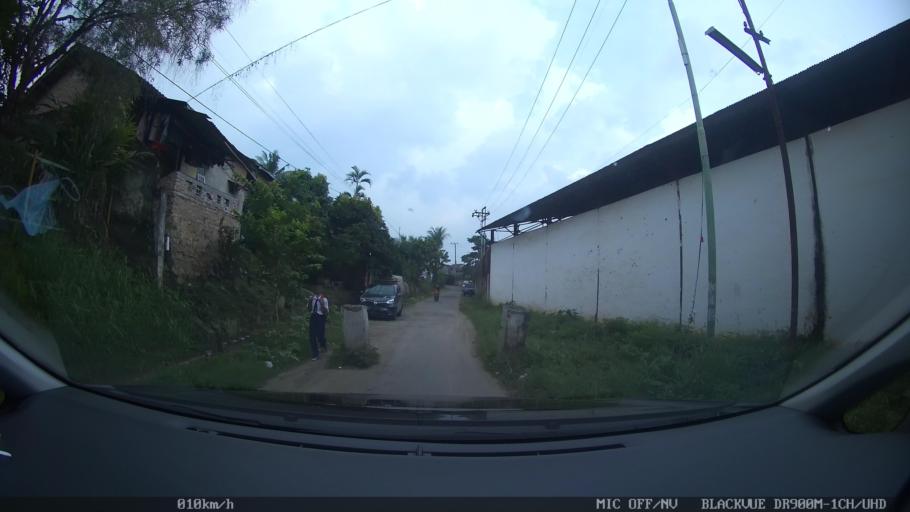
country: ID
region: Lampung
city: Bandarlampung
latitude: -5.4369
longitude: 105.2915
